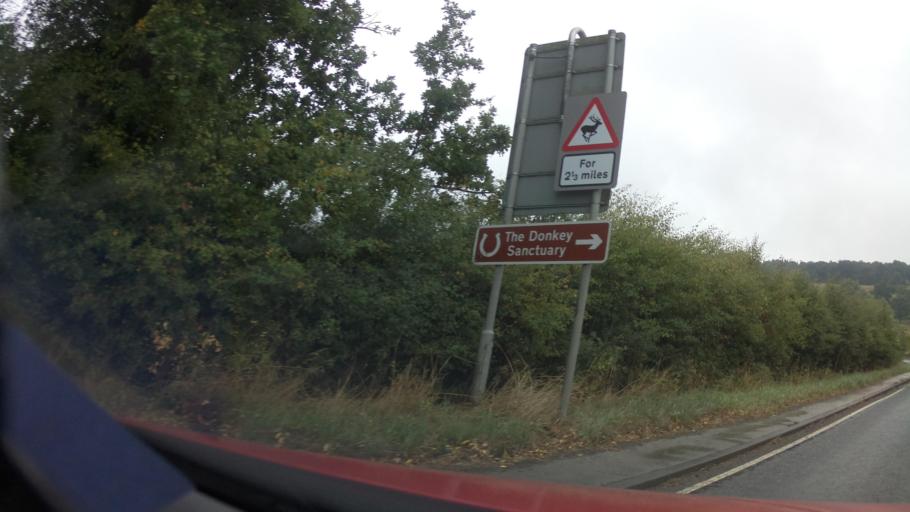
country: GB
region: England
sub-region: North Yorkshire
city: Pannal
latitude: 53.9082
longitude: -1.5261
